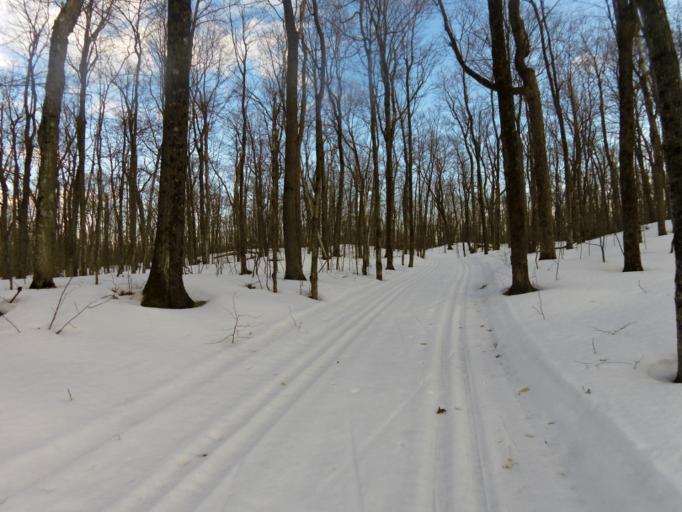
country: CA
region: Quebec
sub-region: Outaouais
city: Gatineau
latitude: 45.4759
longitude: -75.8413
